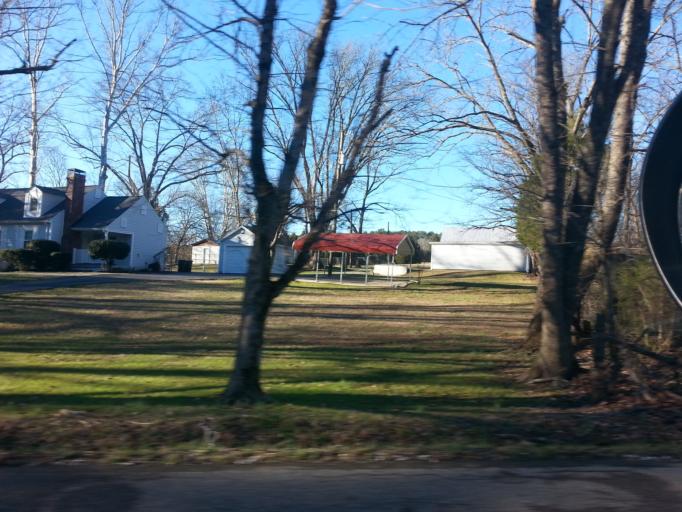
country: US
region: Tennessee
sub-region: Knox County
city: Knoxville
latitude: 35.8820
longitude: -83.9125
